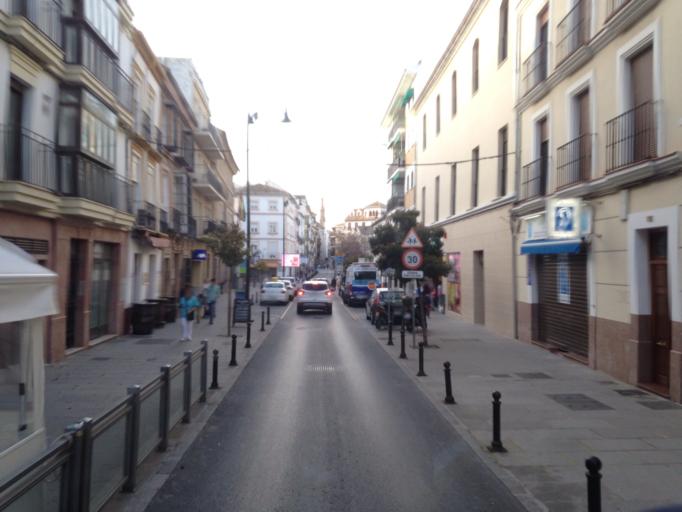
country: ES
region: Andalusia
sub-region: Provincia de Malaga
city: Antequera
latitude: 37.0180
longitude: -4.5577
